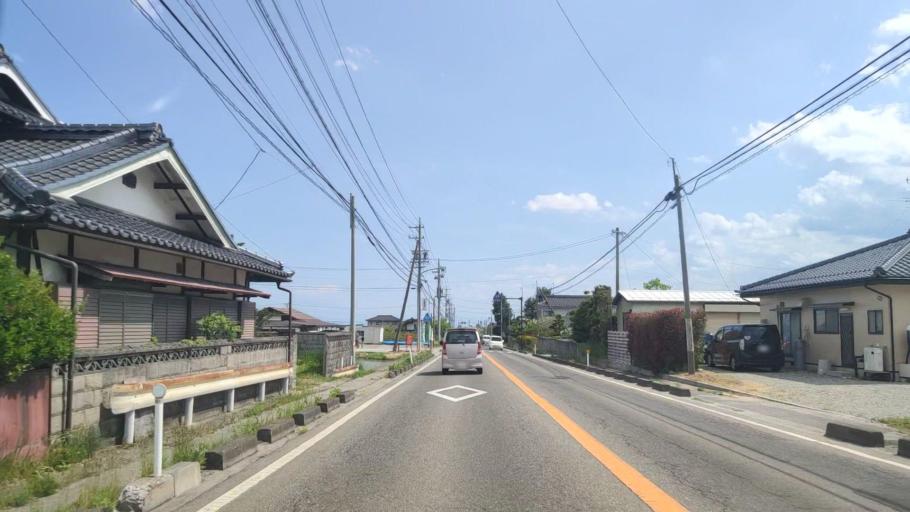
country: JP
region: Nagano
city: Omachi
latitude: 36.4553
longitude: 137.8515
